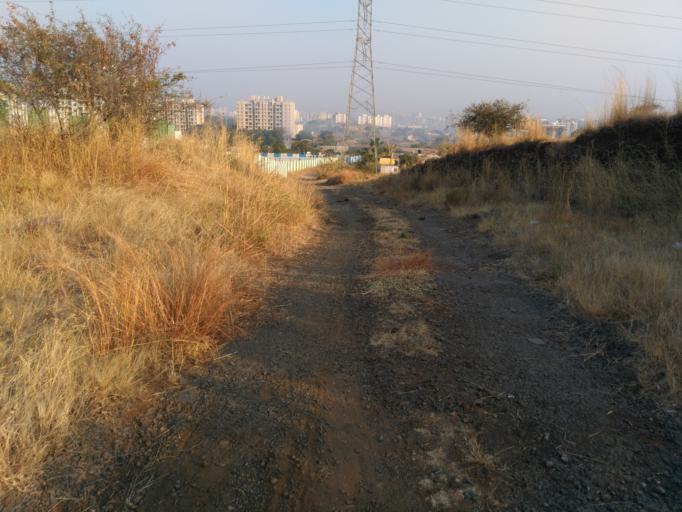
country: IN
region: Maharashtra
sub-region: Pune Division
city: Pune
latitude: 18.4308
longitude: 73.9015
